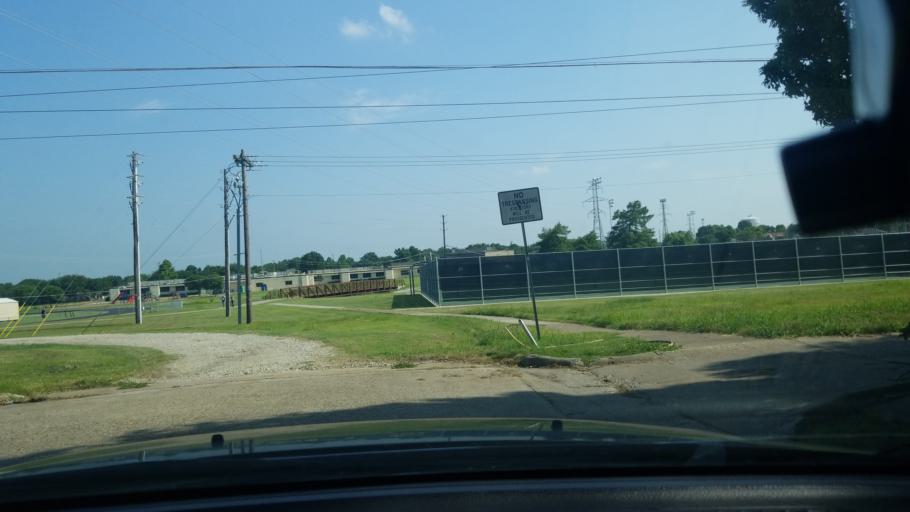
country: US
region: Texas
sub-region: Dallas County
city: Mesquite
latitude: 32.8198
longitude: -96.6118
